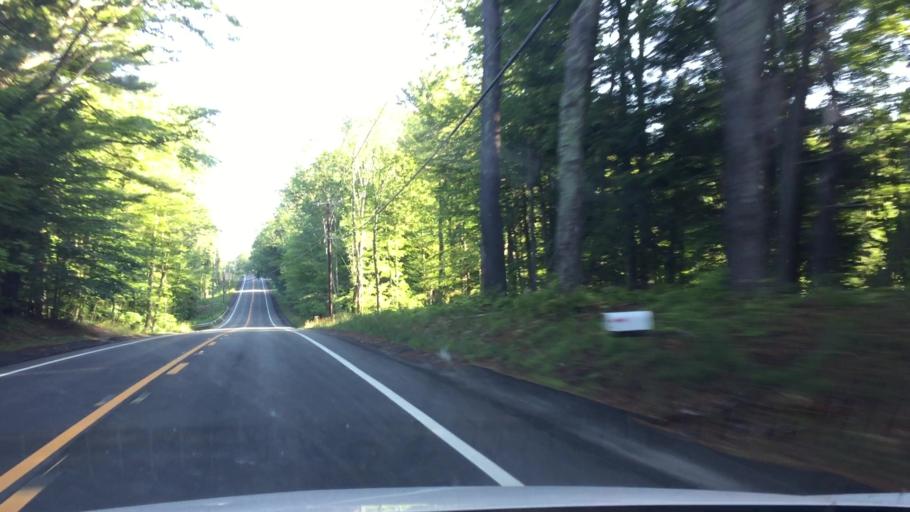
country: US
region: Massachusetts
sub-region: Berkshire County
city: Becket
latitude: 42.2695
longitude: -73.0529
